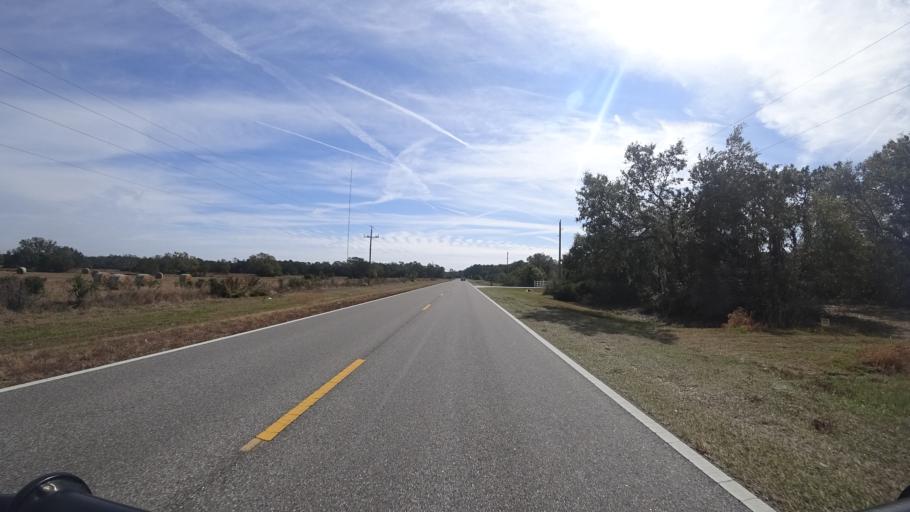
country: US
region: Florida
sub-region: Hillsborough County
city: Sun City Center
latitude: 27.5617
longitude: -82.3733
